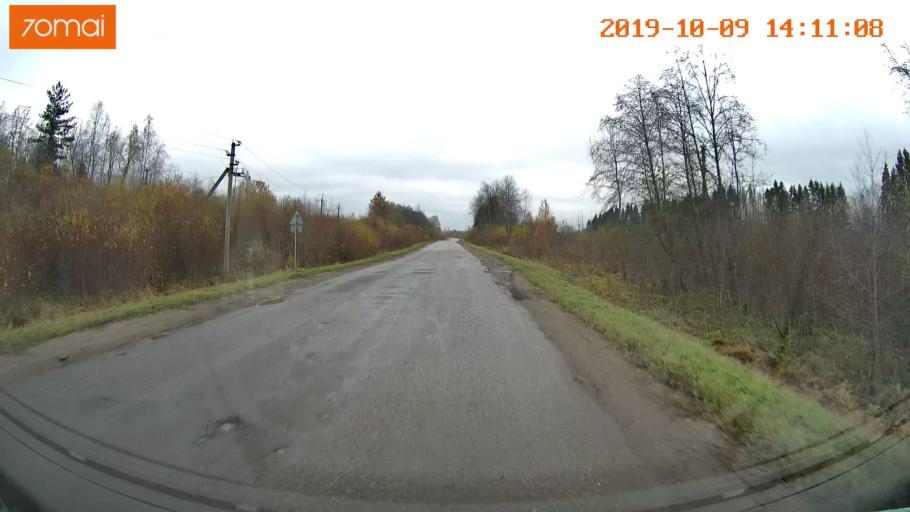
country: RU
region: Kostroma
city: Buy
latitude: 58.4825
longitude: 41.4821
